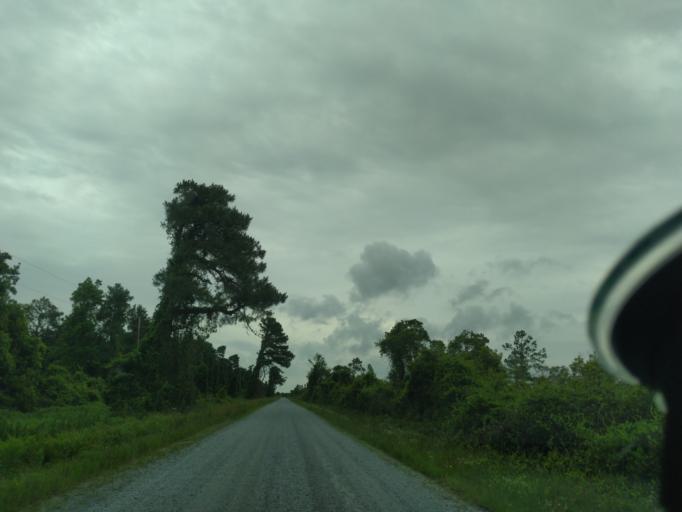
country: US
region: North Carolina
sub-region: Beaufort County
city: Belhaven
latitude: 35.7354
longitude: -76.4583
